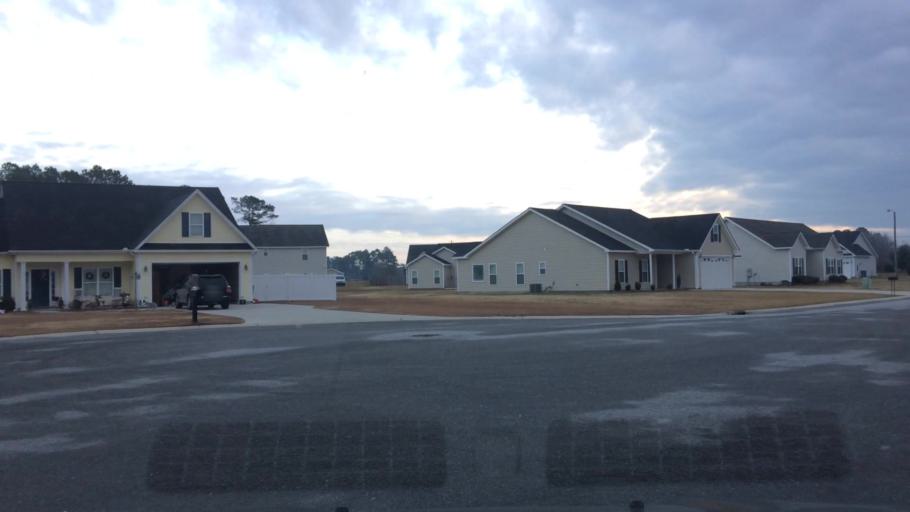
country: US
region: North Carolina
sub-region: Pitt County
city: Ayden
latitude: 35.4686
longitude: -77.4381
